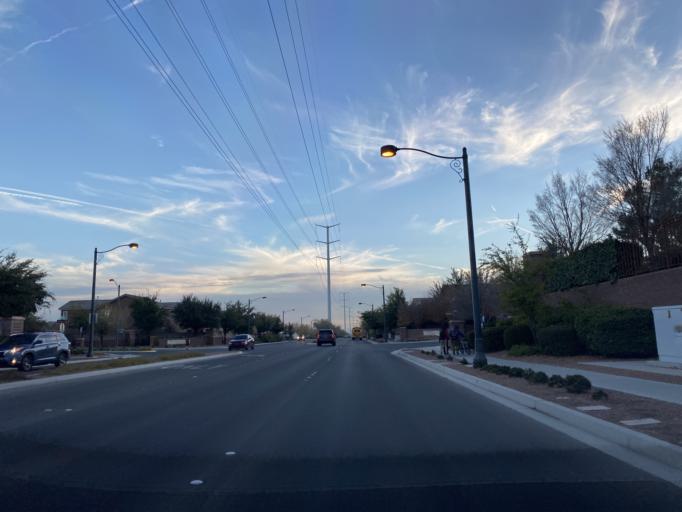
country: US
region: Nevada
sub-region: Clark County
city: Summerlin South
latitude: 36.2952
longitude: -115.3290
